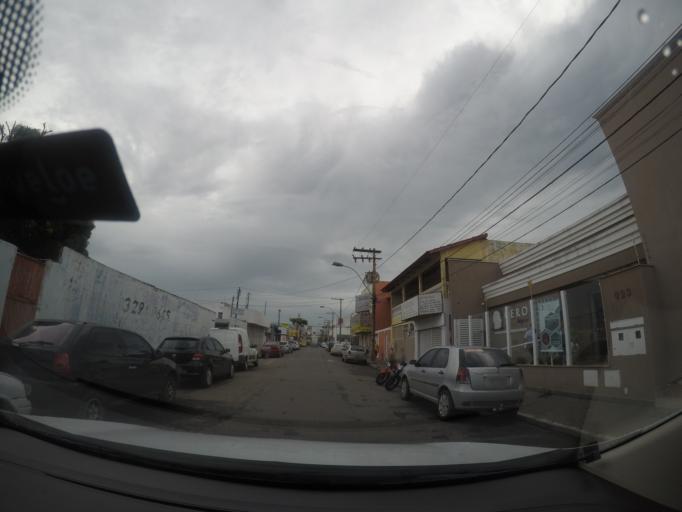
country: BR
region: Goias
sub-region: Goiania
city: Goiania
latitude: -16.6682
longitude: -49.2895
